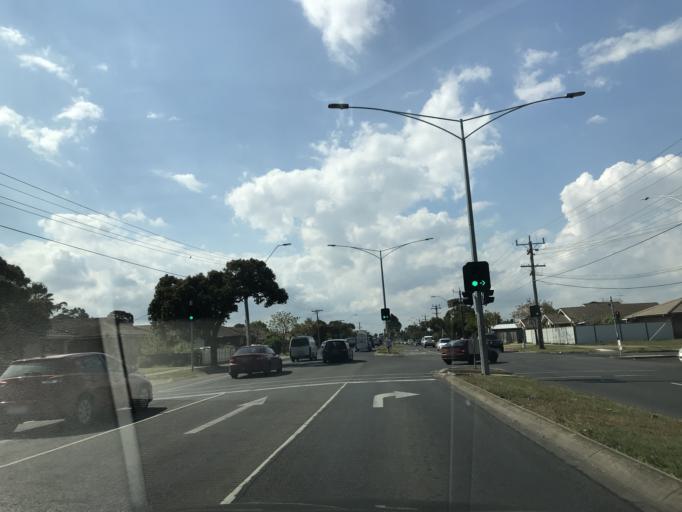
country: AU
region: Victoria
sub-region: Wyndham
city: Hoppers Crossing
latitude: -37.8746
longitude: 144.7021
